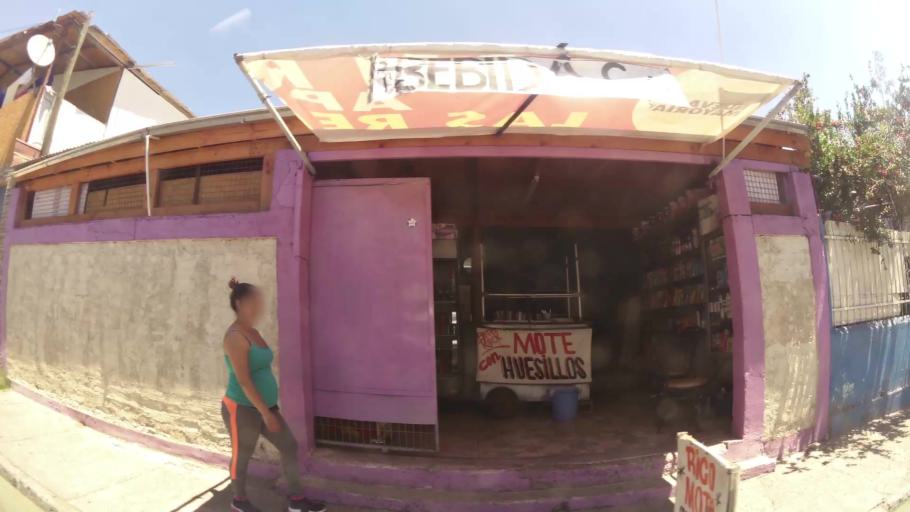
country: CL
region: Santiago Metropolitan
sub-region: Provincia de Santiago
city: La Pintana
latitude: -33.5549
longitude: -70.6472
